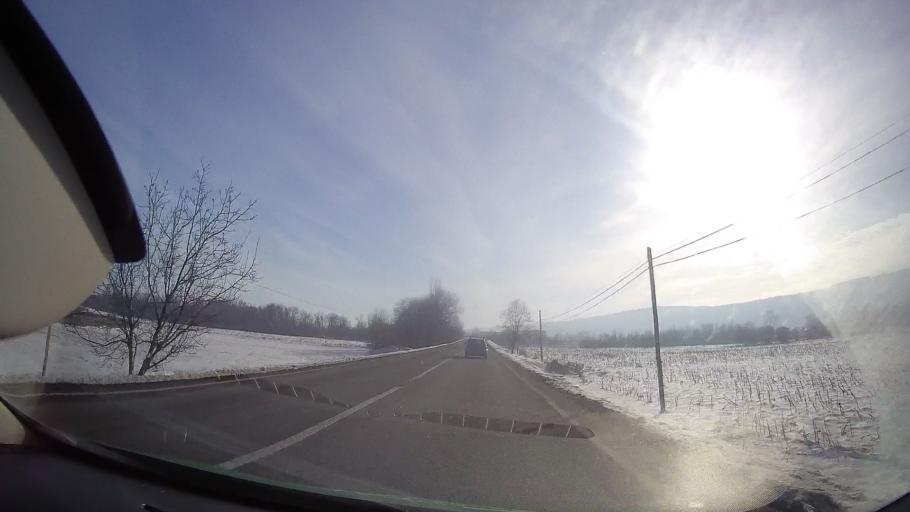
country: RO
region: Neamt
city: Bodesti
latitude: 47.0498
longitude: 26.4034
